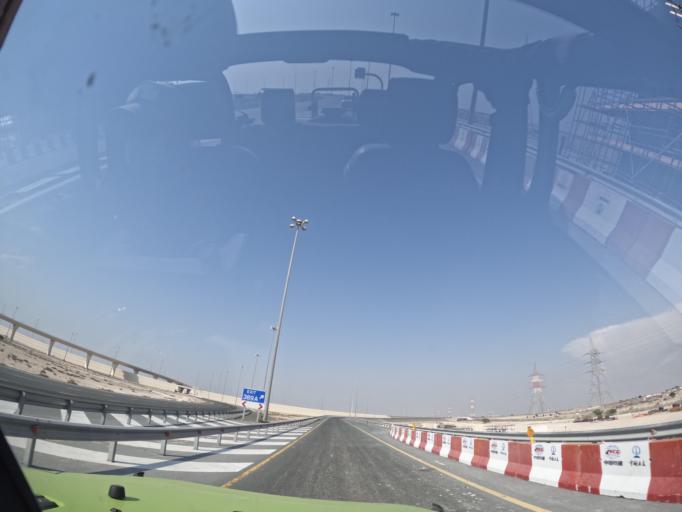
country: AE
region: Abu Dhabi
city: Abu Dhabi
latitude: 24.6749
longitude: 54.8222
